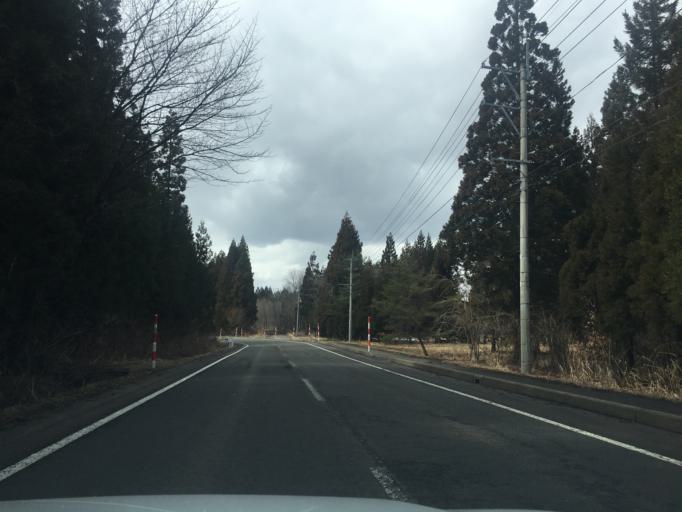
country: JP
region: Akita
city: Takanosu
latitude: 40.1799
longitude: 140.3547
